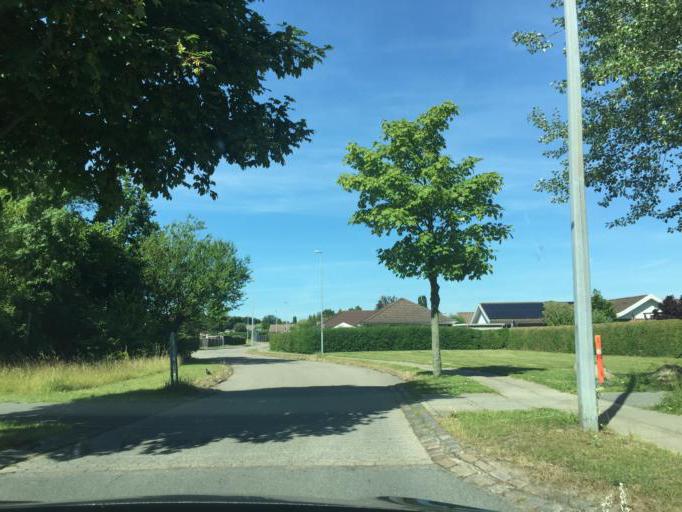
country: DK
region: South Denmark
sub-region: Odense Kommune
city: Neder Holluf
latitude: 55.3707
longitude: 10.4716
